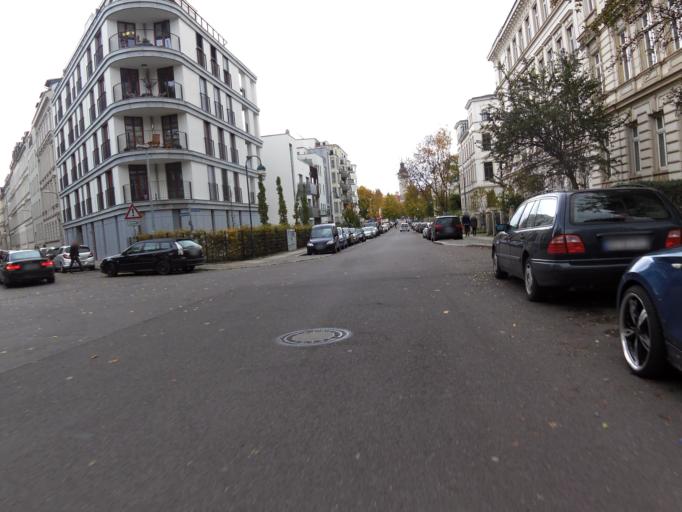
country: DE
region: Saxony
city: Leipzig
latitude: 51.3411
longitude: 12.3623
